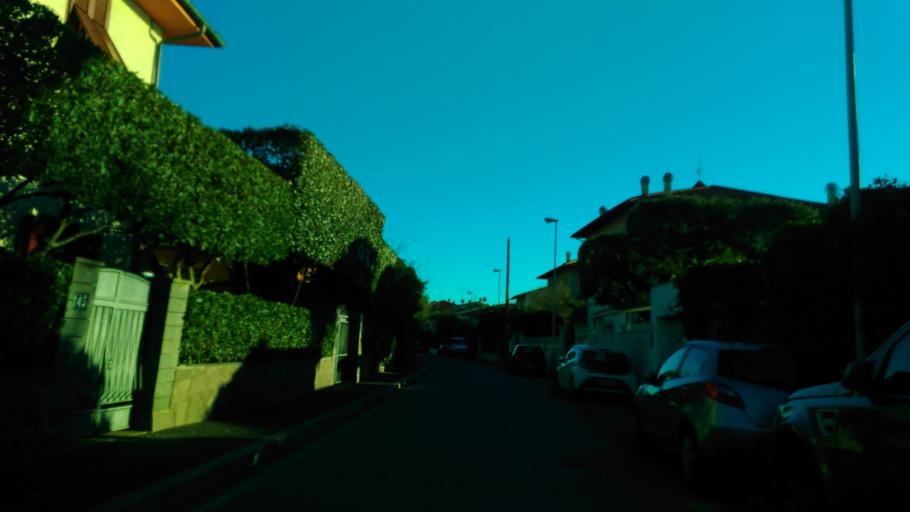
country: IT
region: Tuscany
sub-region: Provincia di Livorno
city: Quercianella
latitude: 43.4528
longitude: 10.3740
